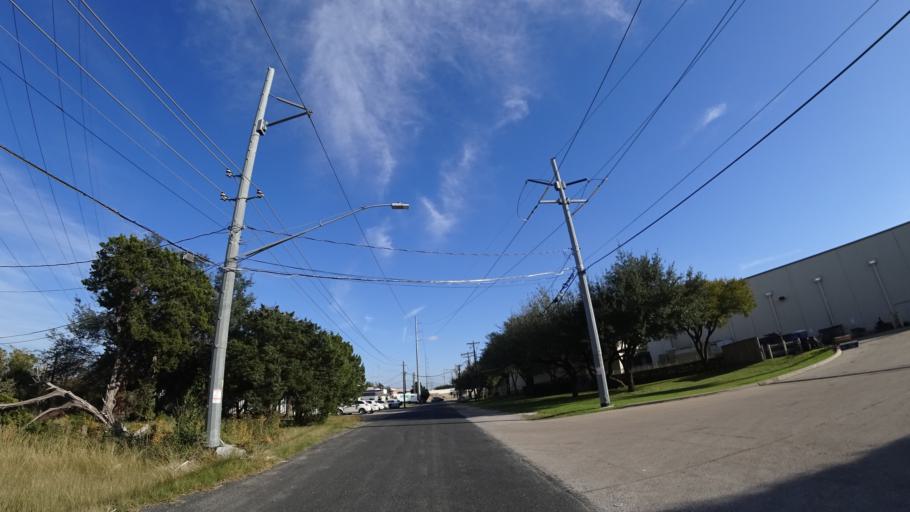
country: US
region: Texas
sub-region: Williamson County
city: Jollyville
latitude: 30.4029
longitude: -97.7476
